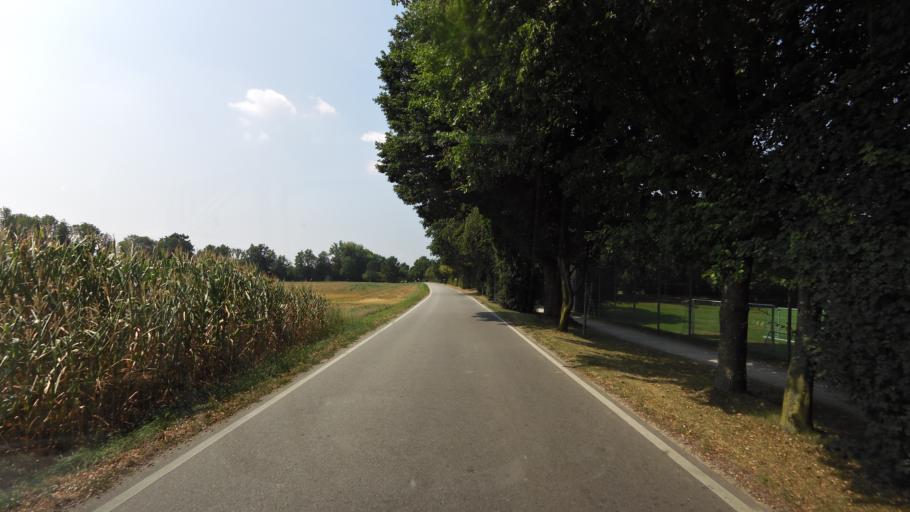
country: DE
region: Bavaria
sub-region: Lower Bavaria
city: Bad Fussing
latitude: 48.3444
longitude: 13.3175
